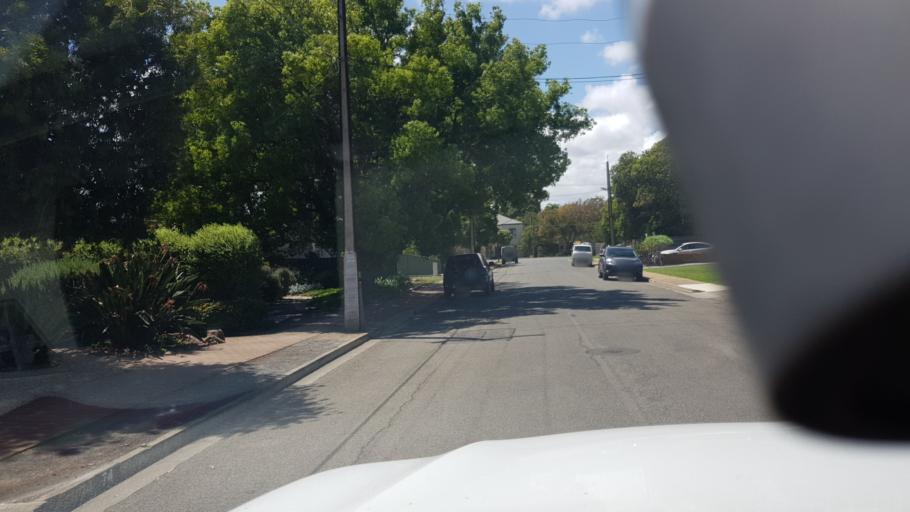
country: AU
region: South Australia
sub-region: Holdfast Bay
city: North Brighton
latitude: -35.0068
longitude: 138.5298
